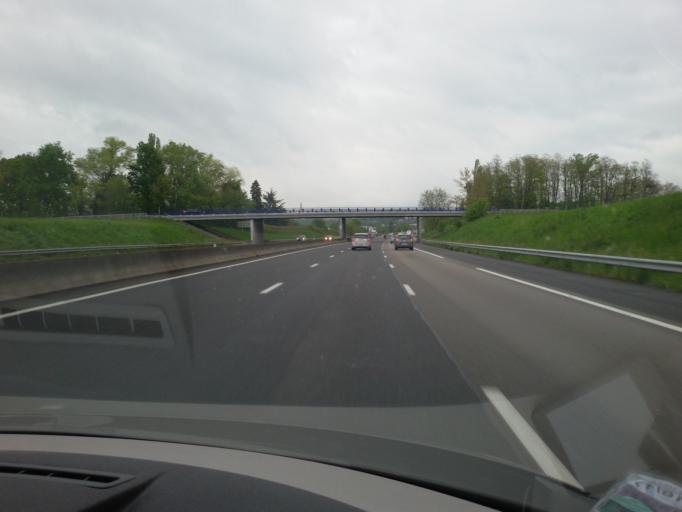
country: FR
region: Bourgogne
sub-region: Departement de Saone-et-Loire
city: Creches-sur-Saone
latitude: 46.2747
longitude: 4.7878
